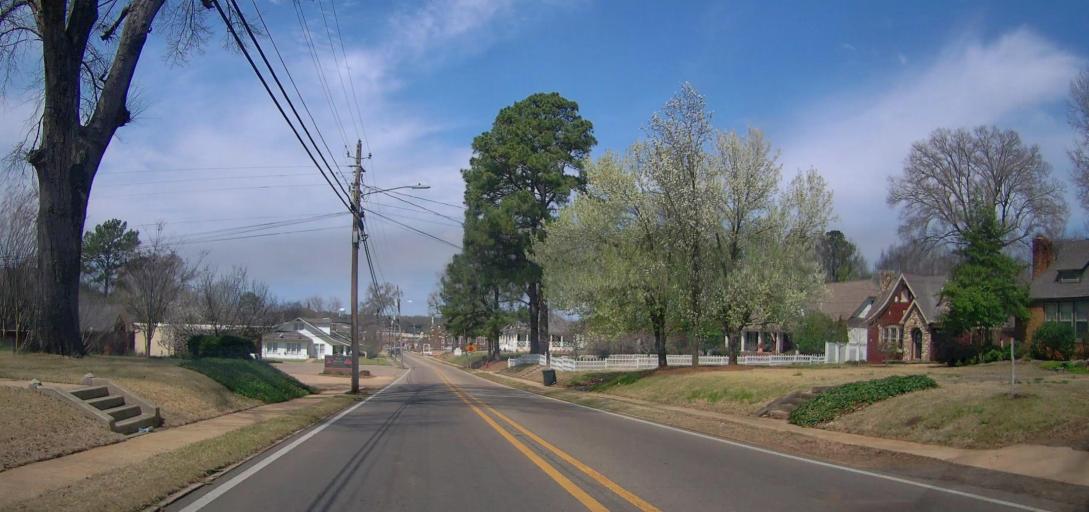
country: US
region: Mississippi
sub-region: Union County
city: New Albany
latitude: 34.4901
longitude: -89.0038
